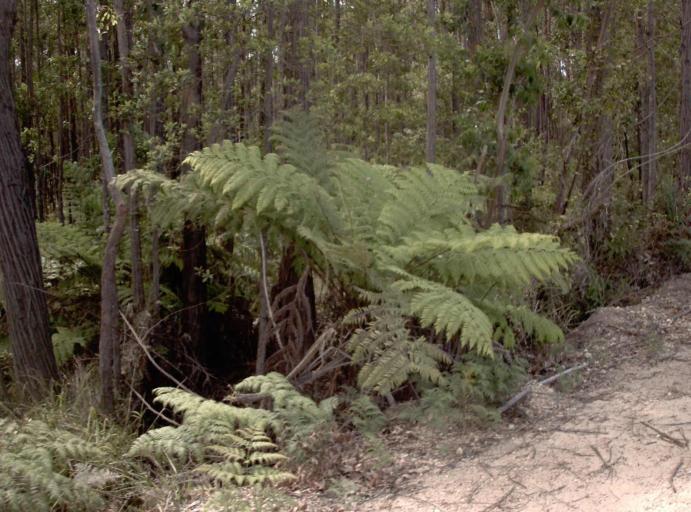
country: AU
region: Victoria
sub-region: East Gippsland
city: Lakes Entrance
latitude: -37.6239
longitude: 148.6782
